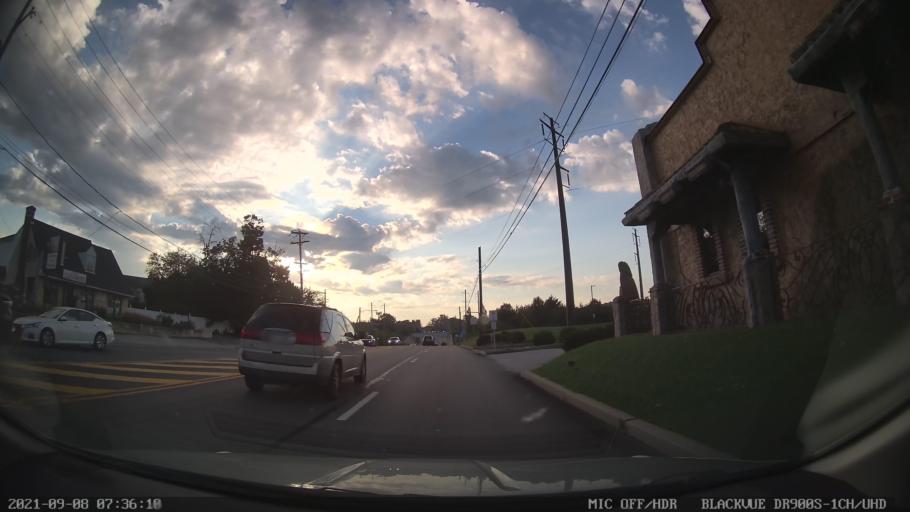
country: US
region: Pennsylvania
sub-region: Montgomery County
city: King of Prussia
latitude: 40.0843
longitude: -75.3870
